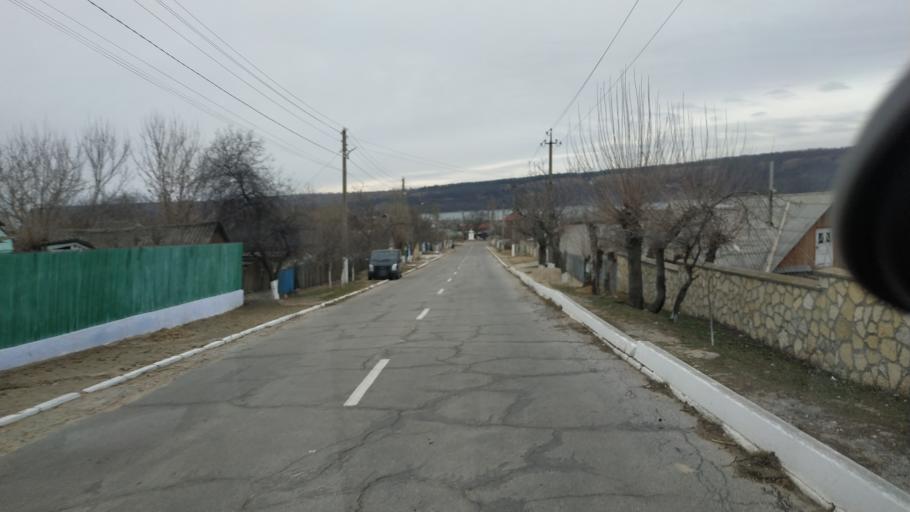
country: MD
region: Telenesti
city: Cocieri
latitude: 47.3436
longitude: 29.1183
